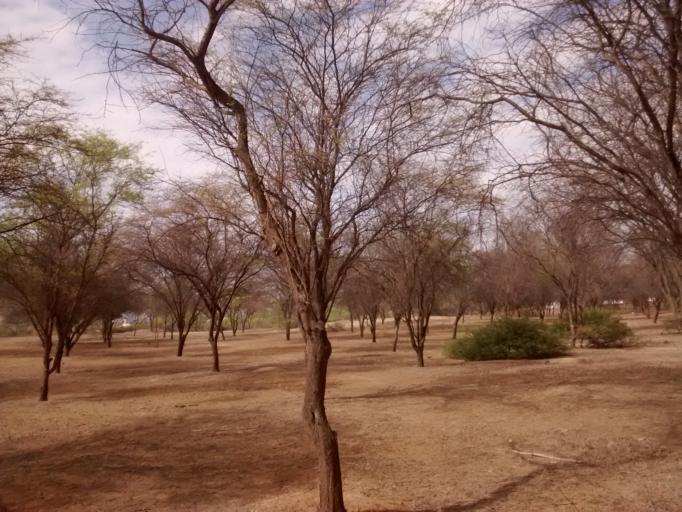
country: PE
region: Piura
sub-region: Provincia de Piura
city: Piura
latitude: -5.1794
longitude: -80.6353
